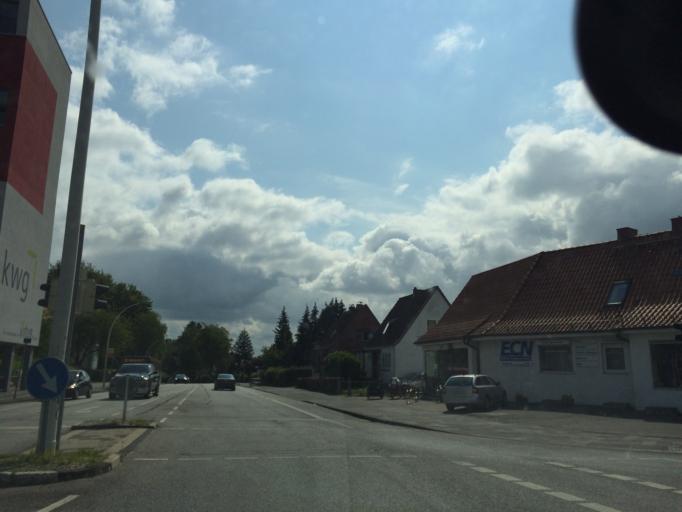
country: DE
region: Schleswig-Holstein
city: Kronshagen
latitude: 54.3170
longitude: 10.0664
